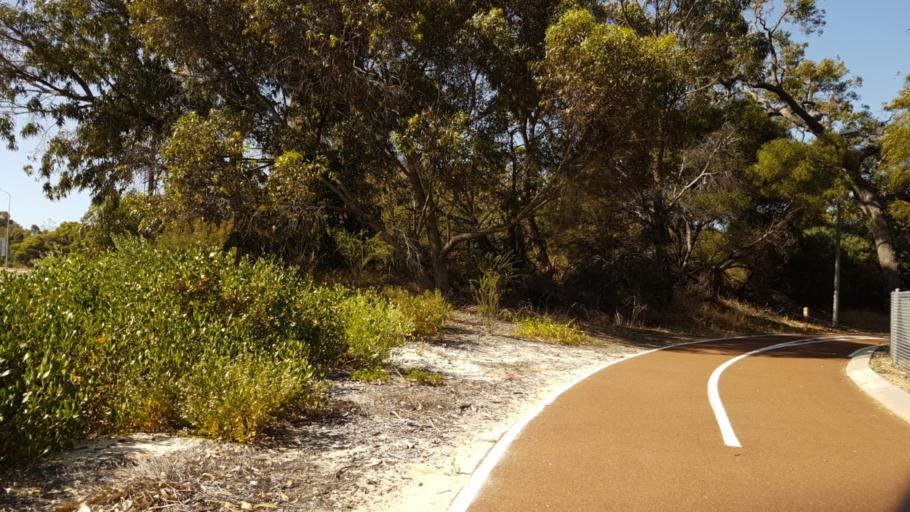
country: AU
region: Western Australia
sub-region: Stirling
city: Stirling
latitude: -31.8559
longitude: 115.8023
